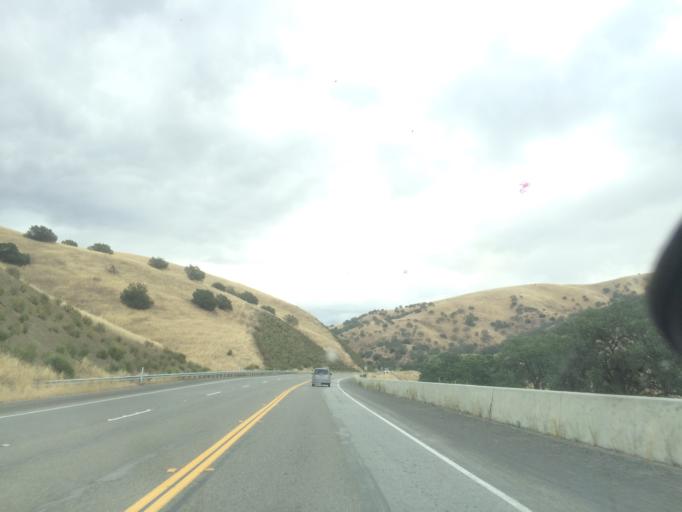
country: US
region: California
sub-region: San Luis Obispo County
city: Shandon
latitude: 35.7809
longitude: -120.1976
